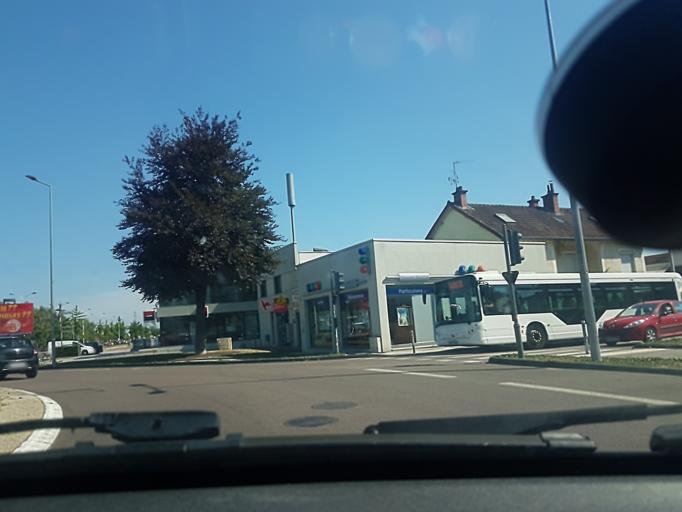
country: FR
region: Bourgogne
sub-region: Departement de Saone-et-Loire
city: Chalon-sur-Saone
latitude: 46.7904
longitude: 4.8620
